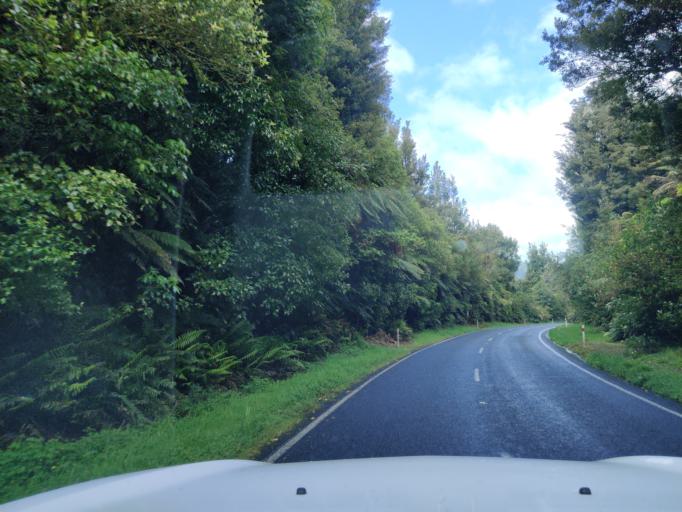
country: NZ
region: Bay of Plenty
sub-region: Rotorua District
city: Rotorua
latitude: -38.1802
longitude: 176.3267
